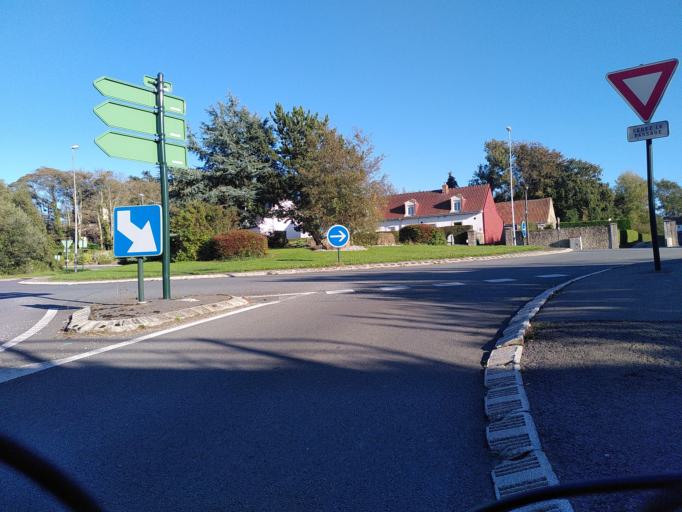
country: FR
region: Nord-Pas-de-Calais
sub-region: Departement du Pas-de-Calais
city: La Capelle-les-Boulogne
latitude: 50.7342
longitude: 1.6805
